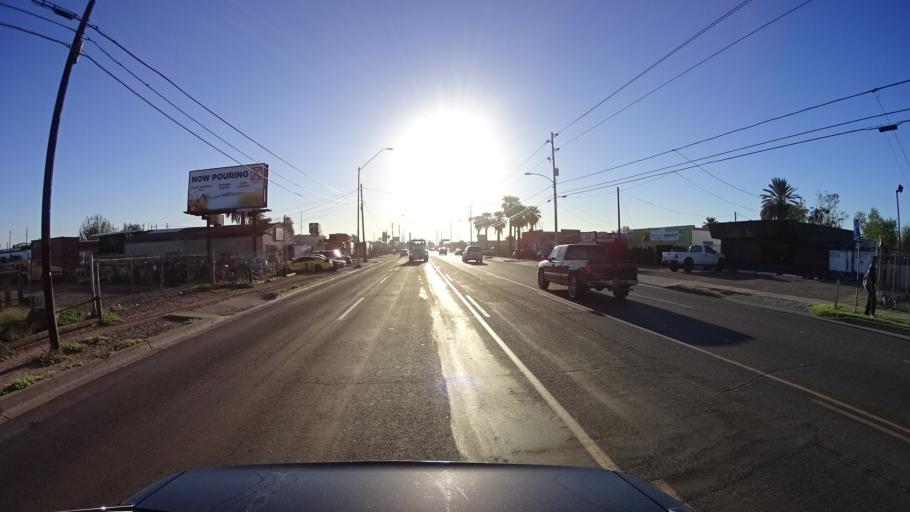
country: US
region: Arizona
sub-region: Maricopa County
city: Phoenix
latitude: 33.4369
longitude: -112.1212
